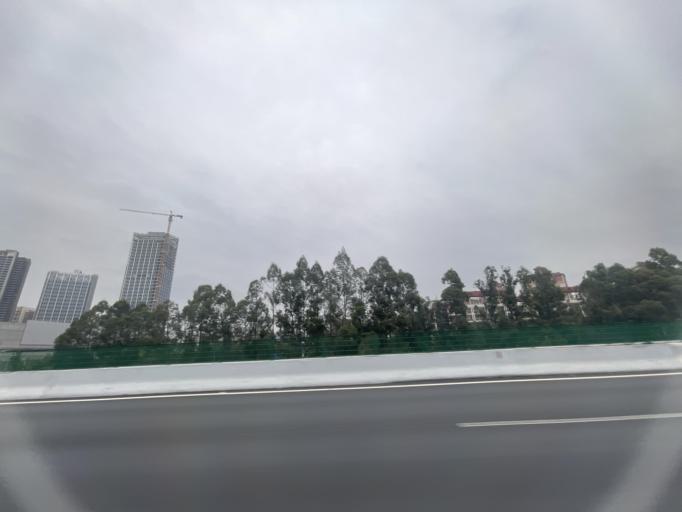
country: CN
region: Guangdong
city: Huangge
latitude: 22.7894
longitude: 113.5164
